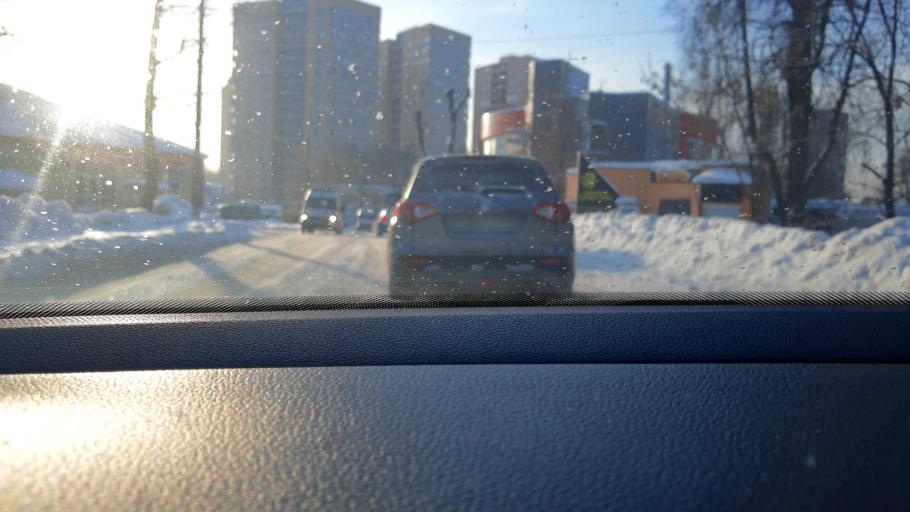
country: RU
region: Moskovskaya
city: Lesnyye Polyany
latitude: 55.9431
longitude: 37.8683
